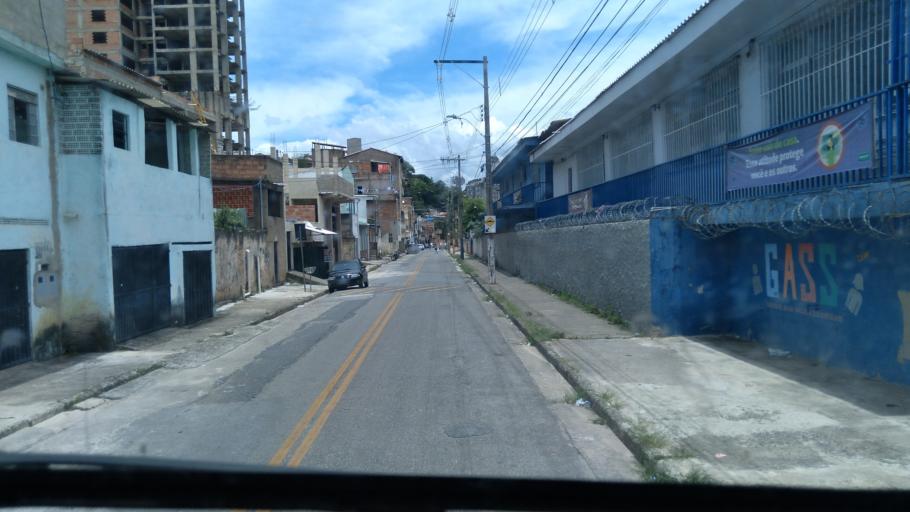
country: BR
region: Minas Gerais
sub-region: Belo Horizonte
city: Belo Horizonte
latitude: -19.9192
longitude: -43.9222
